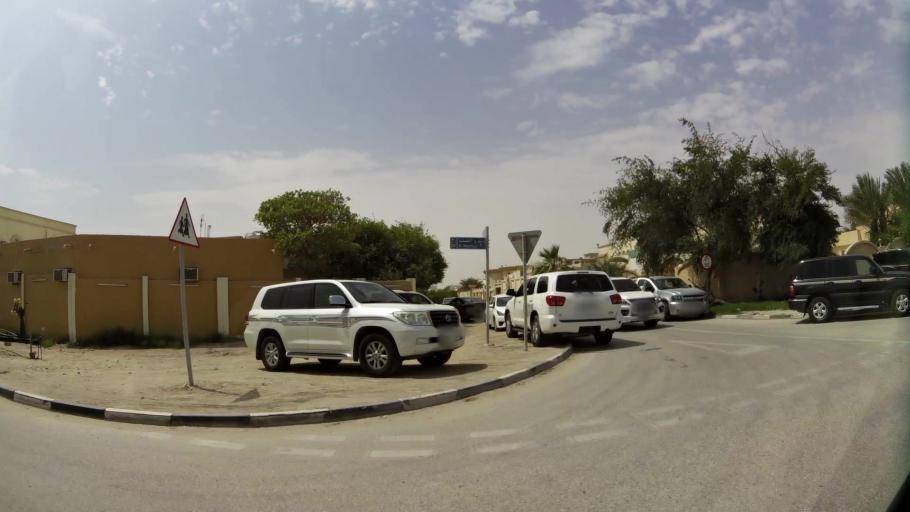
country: QA
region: Baladiyat ar Rayyan
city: Ar Rayyan
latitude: 25.3545
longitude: 51.4764
